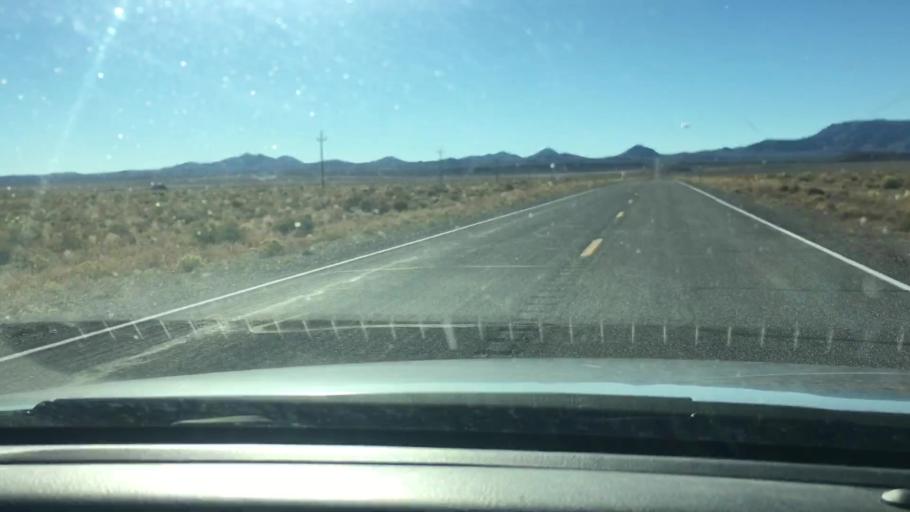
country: US
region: Nevada
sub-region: Nye County
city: Tonopah
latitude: 38.1465
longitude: -116.6045
